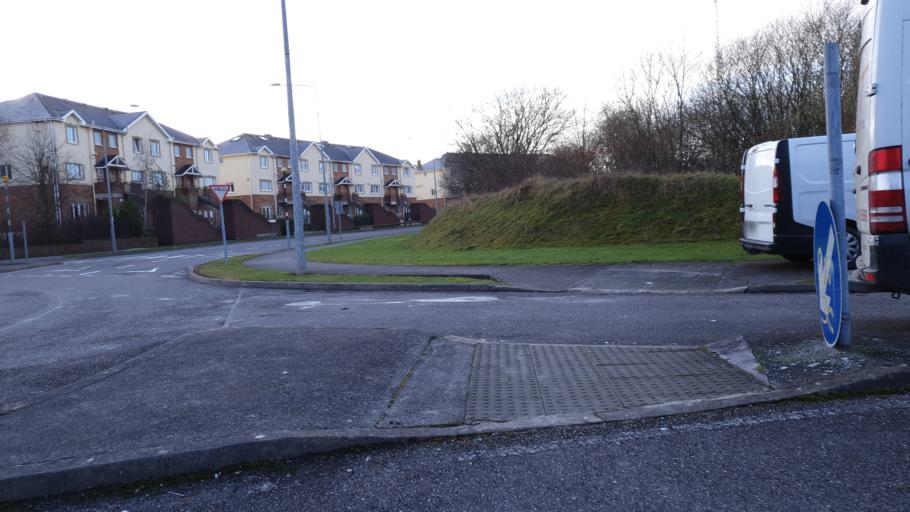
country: IE
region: Munster
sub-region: County Cork
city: Passage West
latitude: 51.8824
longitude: -8.3956
